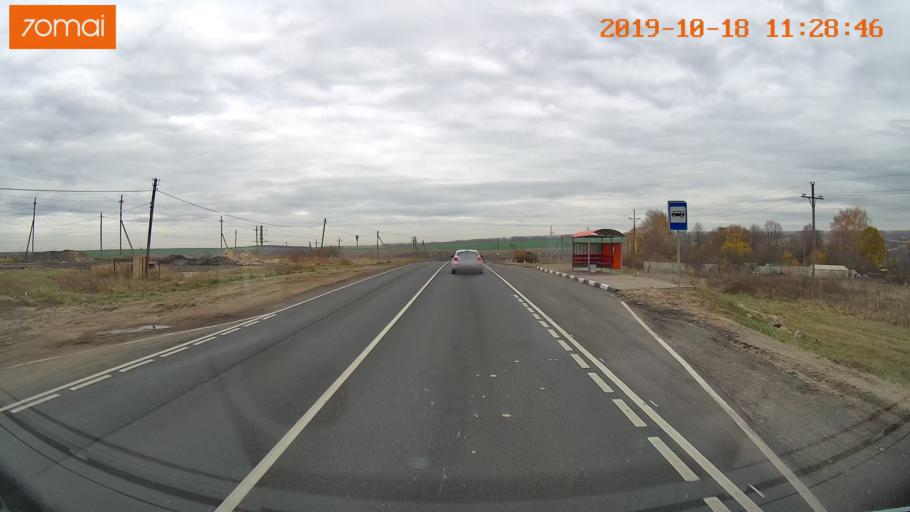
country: RU
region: Tula
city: Kimovsk
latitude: 54.1559
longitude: 38.6651
